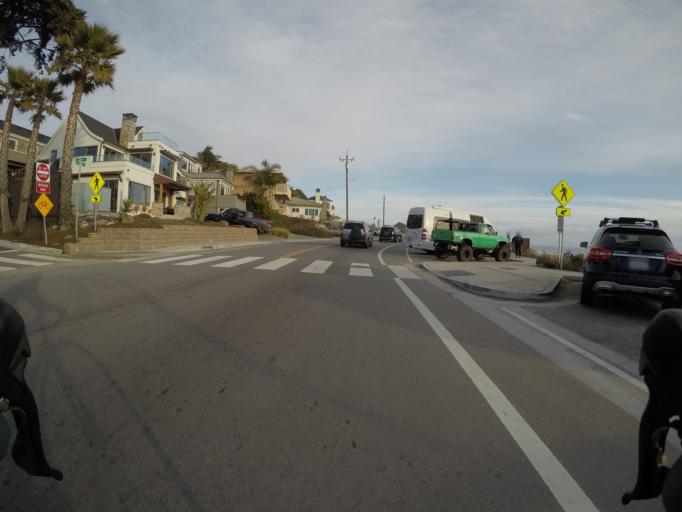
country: US
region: California
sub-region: Santa Cruz County
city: Twin Lakes
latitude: 36.9628
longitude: -121.9999
